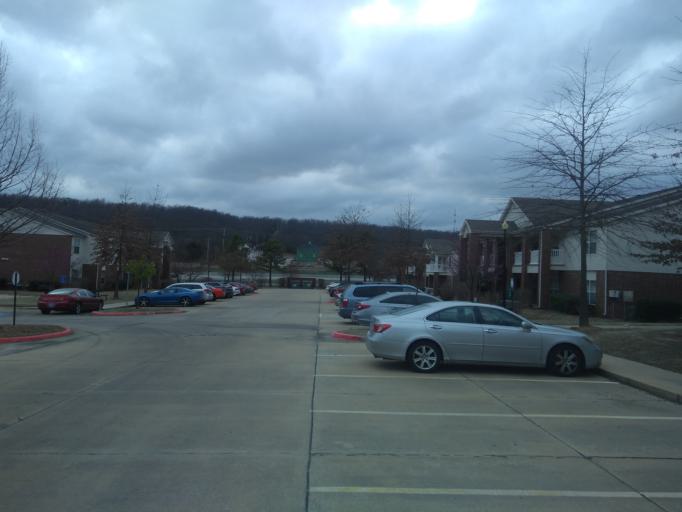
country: US
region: Arkansas
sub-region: Washington County
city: Fayetteville
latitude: 36.0604
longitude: -94.1959
